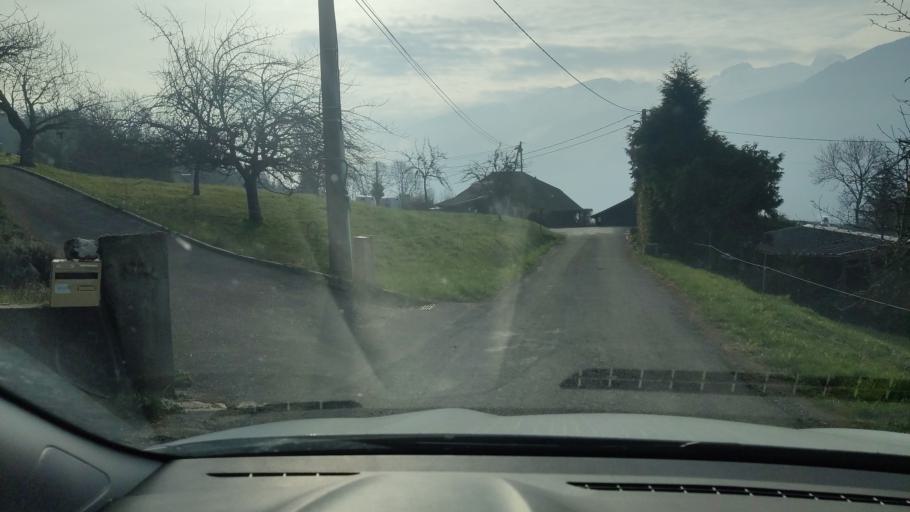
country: FR
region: Rhone-Alpes
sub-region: Departement de la Haute-Savoie
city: Bonneville
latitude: 46.0950
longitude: 6.4081
